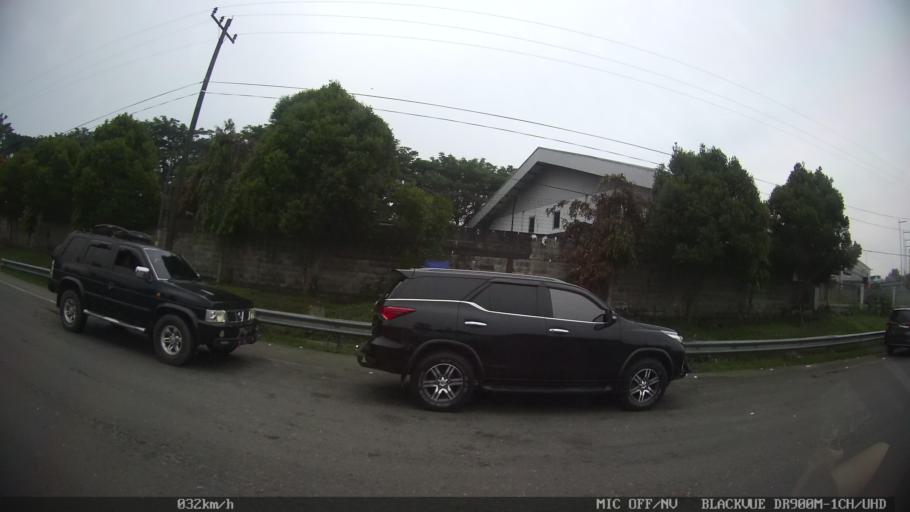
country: ID
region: North Sumatra
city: Deli Tua
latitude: 3.5366
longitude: 98.7217
